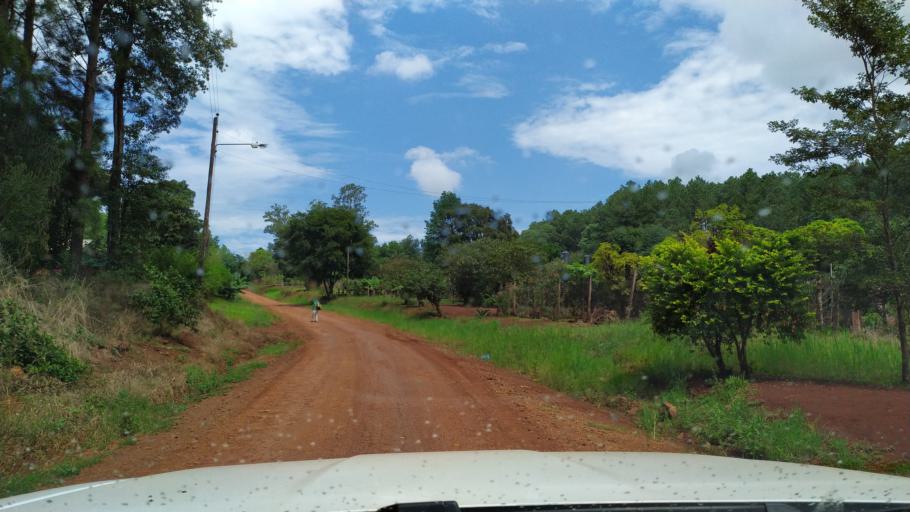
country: AR
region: Misiones
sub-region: Departamento de Eldorado
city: Eldorado
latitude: -26.5007
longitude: -54.5901
